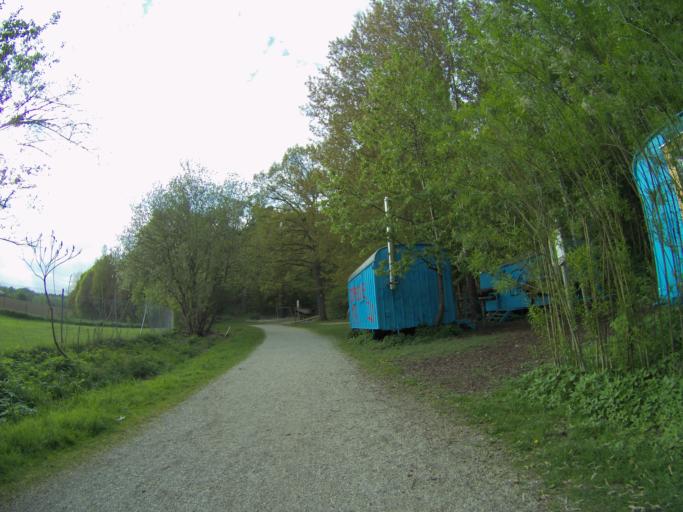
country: DE
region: Bavaria
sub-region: Upper Bavaria
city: Freising
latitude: 48.4136
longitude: 11.7575
